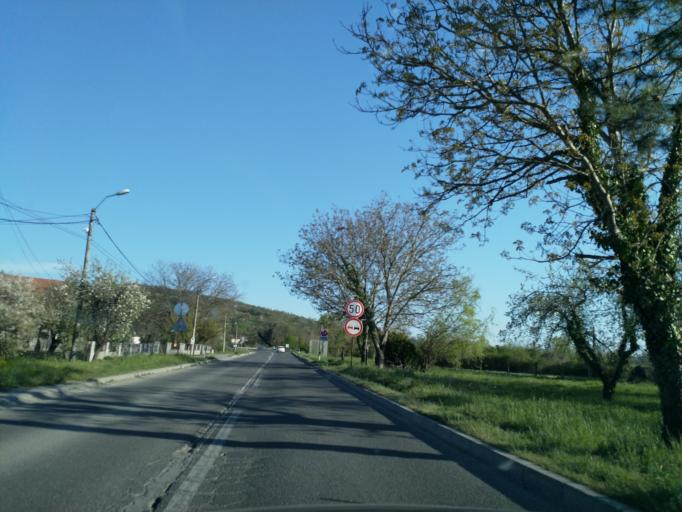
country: RS
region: Central Serbia
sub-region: Kolubarski Okrug
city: Lajkovac
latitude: 44.3693
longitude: 20.1913
